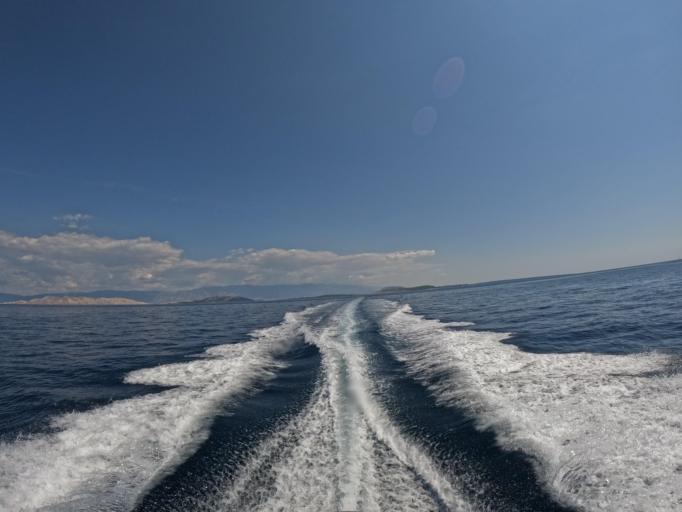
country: HR
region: Primorsko-Goranska
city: Lopar
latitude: 44.8913
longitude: 14.6324
